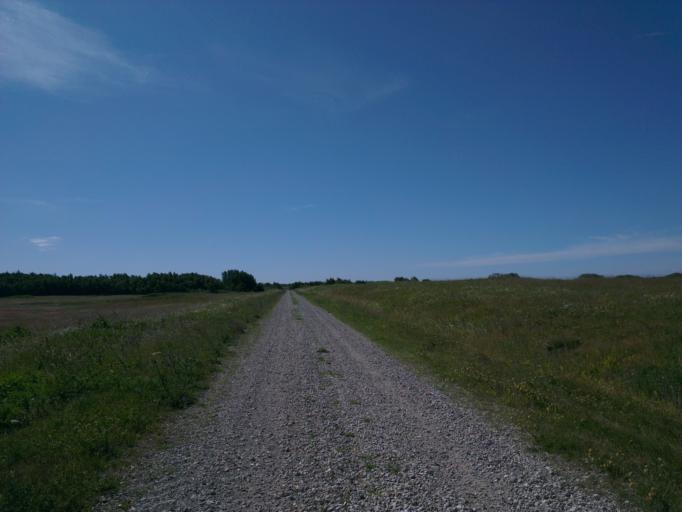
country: DK
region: Capital Region
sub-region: Frederikssund Kommune
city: Jaegerspris
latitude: 55.8876
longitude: 11.9330
